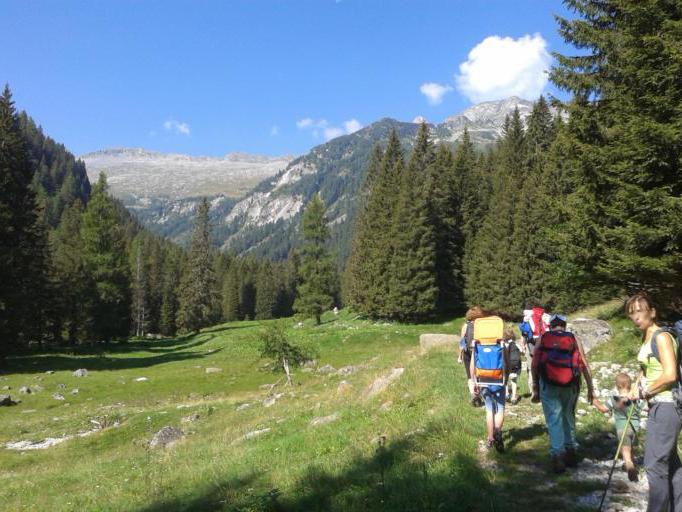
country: IT
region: Lombardy
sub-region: Provincia di Brescia
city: Saviore
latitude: 46.0002
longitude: 10.4995
